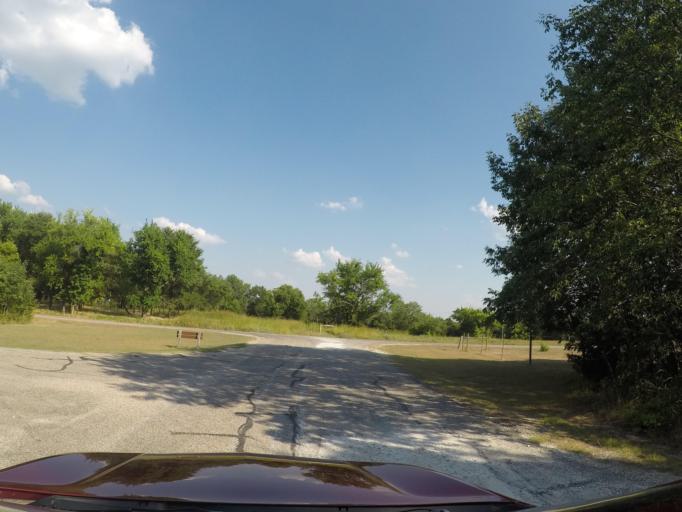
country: US
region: Texas
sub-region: Grayson County
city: Preston
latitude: 33.8230
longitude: -96.6121
